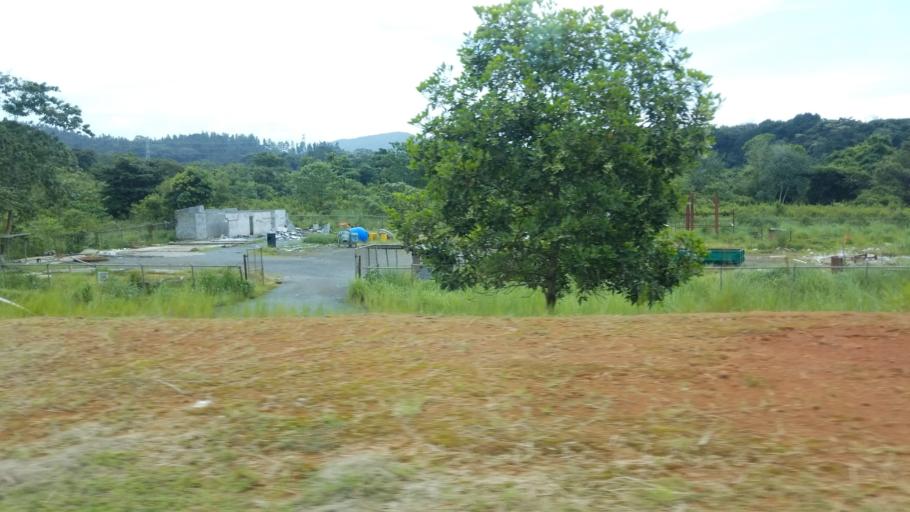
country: PA
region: Panama
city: Las Cumbres
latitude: 9.1091
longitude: -79.4756
